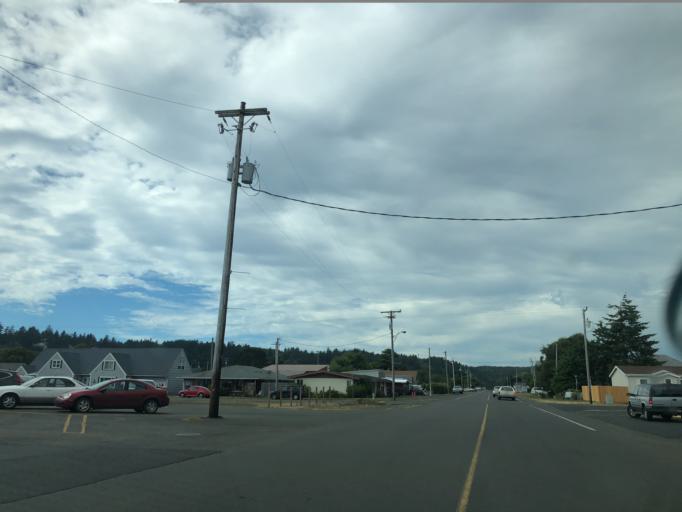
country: US
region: Oregon
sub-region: Lincoln County
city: Waldport
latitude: 44.4300
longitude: -124.0600
